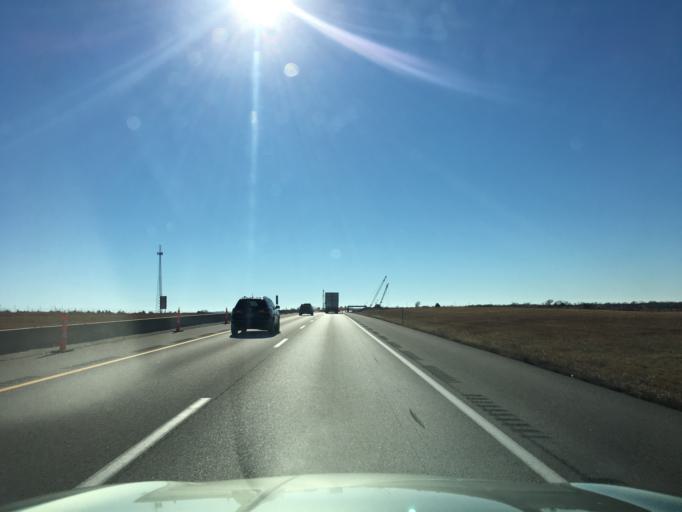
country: US
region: Kansas
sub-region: Sumner County
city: Wellington
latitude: 37.2519
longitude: -97.3390
